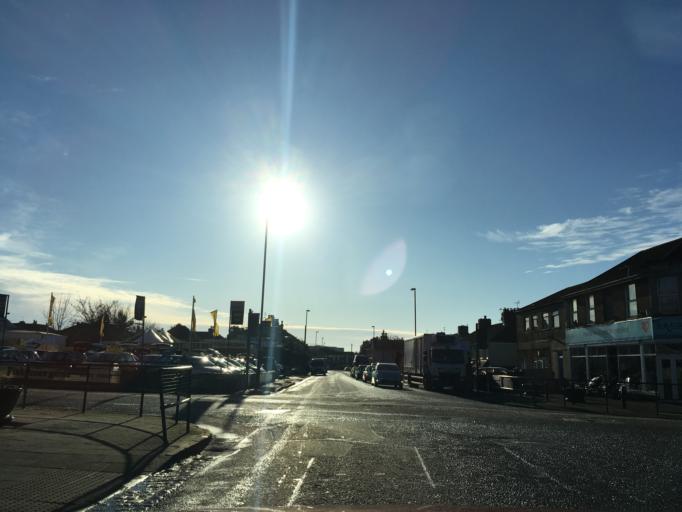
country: GB
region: England
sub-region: South Gloucestershire
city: Mangotsfield
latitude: 51.4730
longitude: -2.5259
